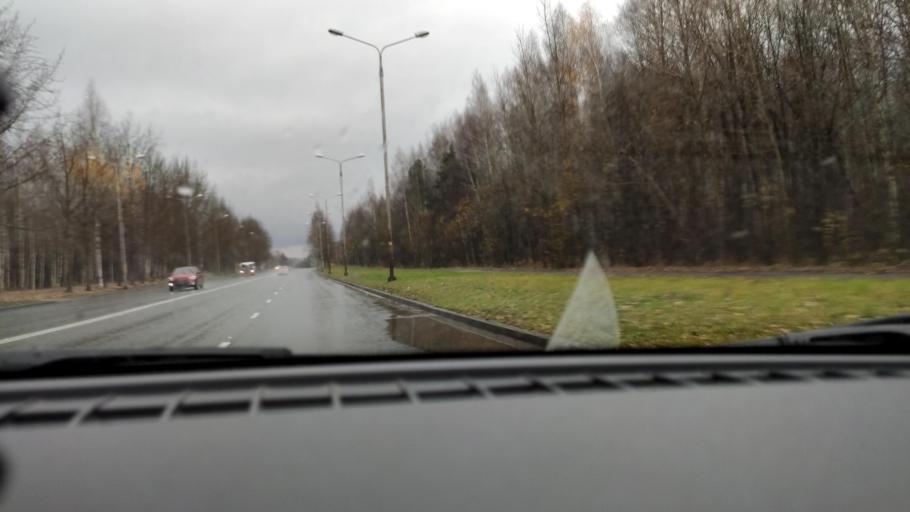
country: RU
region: Perm
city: Perm
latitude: 58.1049
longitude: 56.3935
